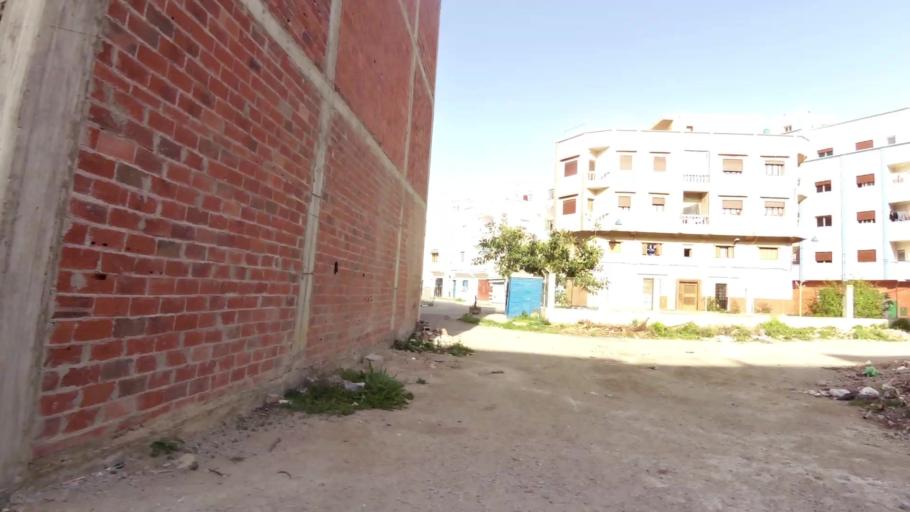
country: MA
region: Tanger-Tetouan
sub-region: Tetouan
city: Martil
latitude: 35.6134
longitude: -5.2803
